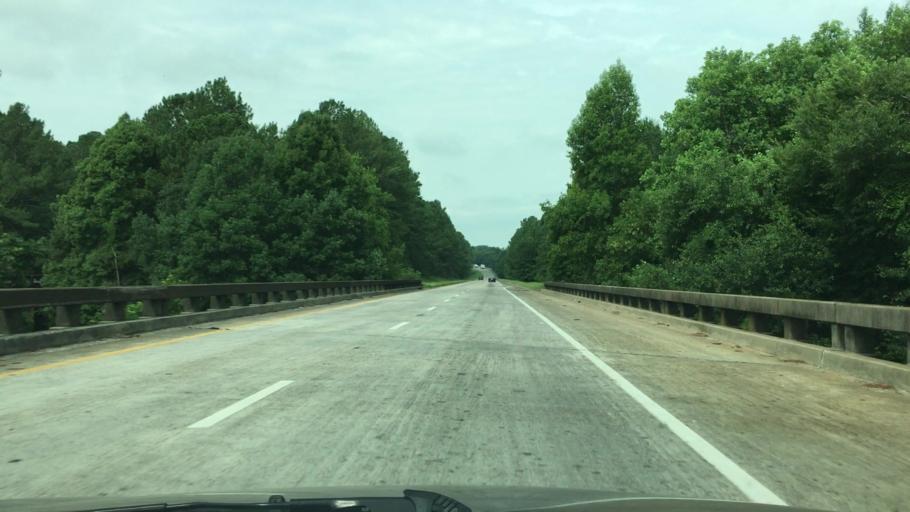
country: US
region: South Carolina
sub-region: Aiken County
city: Graniteville
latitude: 33.6285
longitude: -81.8067
